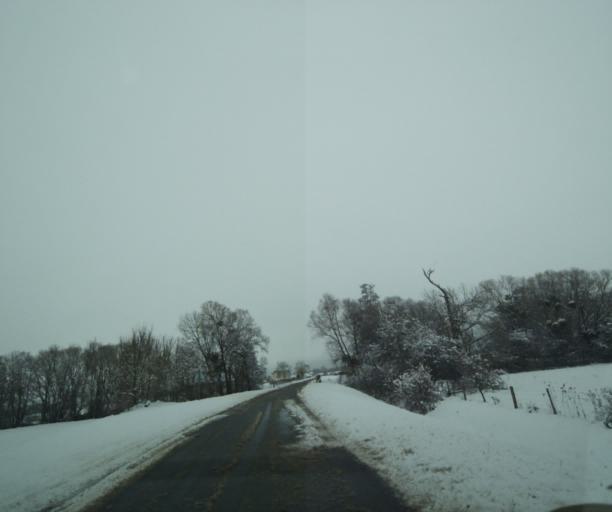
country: FR
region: Champagne-Ardenne
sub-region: Departement de la Haute-Marne
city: Saint-Dizier
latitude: 48.5762
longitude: 4.8915
